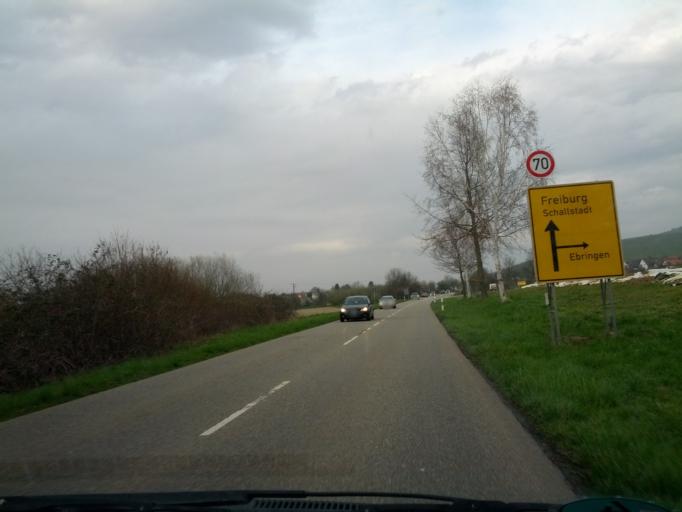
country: DE
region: Baden-Wuerttemberg
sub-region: Freiburg Region
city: Schallstadt
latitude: 47.9544
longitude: 7.7630
